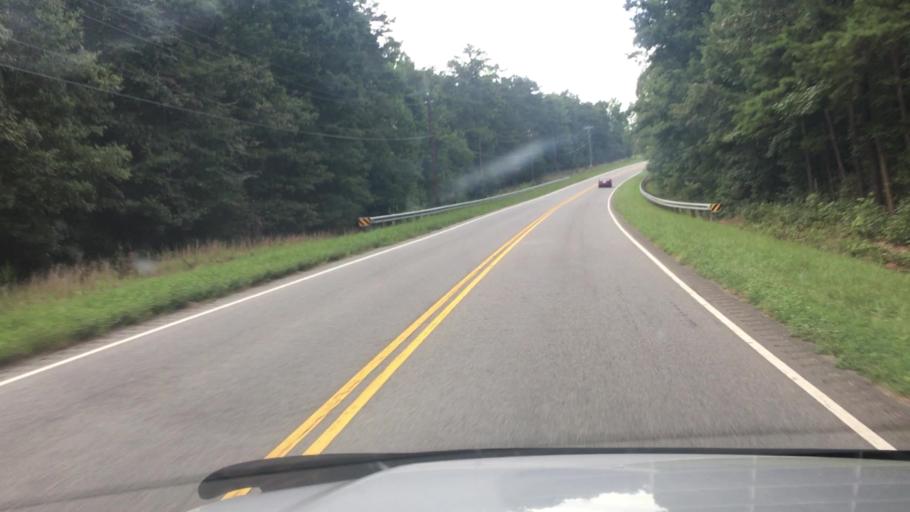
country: US
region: South Carolina
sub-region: Spartanburg County
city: Mayo
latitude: 35.1379
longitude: -81.8216
